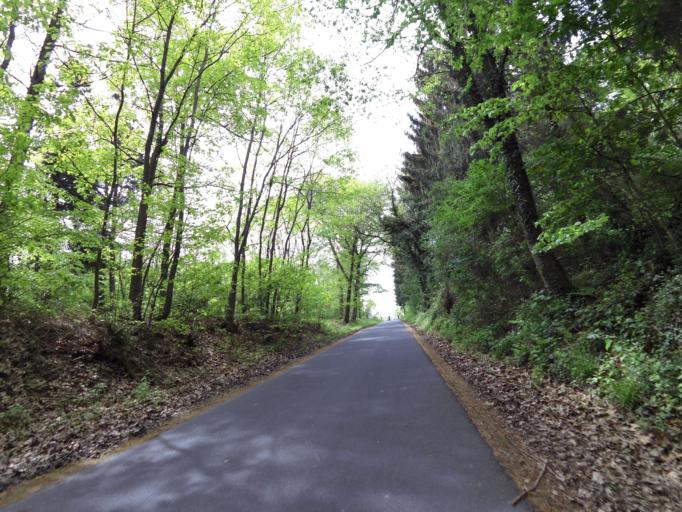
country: DE
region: North Rhine-Westphalia
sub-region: Regierungsbezirk Koln
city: Bonn
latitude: 50.6872
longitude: 7.1118
